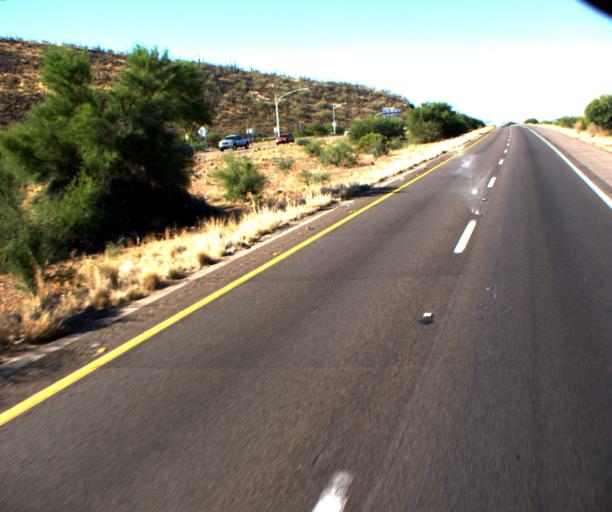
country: US
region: Arizona
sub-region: Pima County
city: Drexel Heights
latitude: 32.1103
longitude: -110.9922
